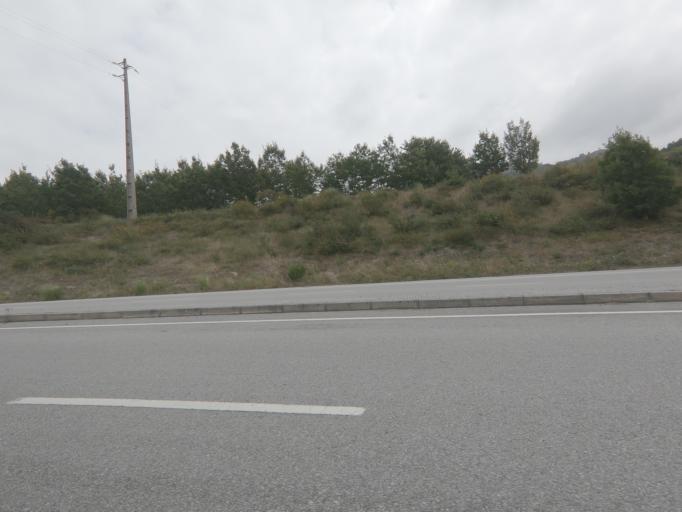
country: PT
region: Viana do Castelo
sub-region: Vila Nova de Cerveira
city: Vila Nova de Cerveira
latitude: 41.9497
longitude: -8.7396
